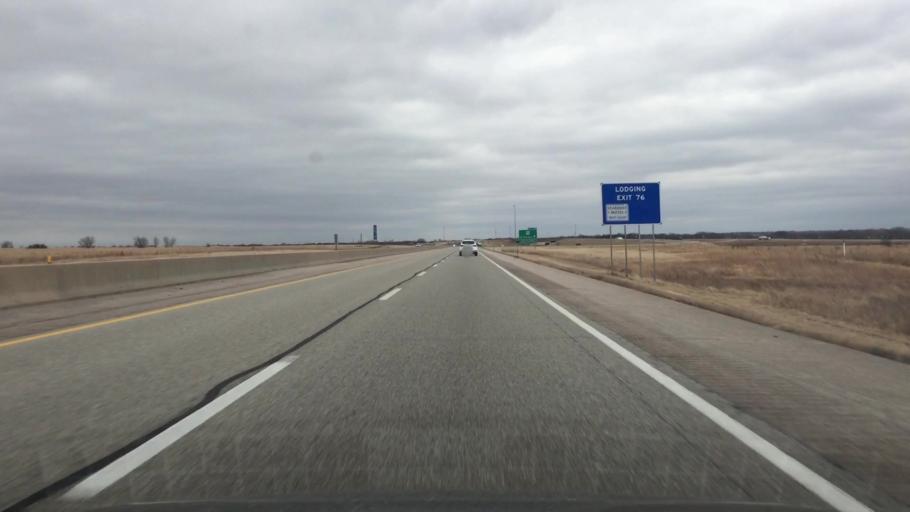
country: US
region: Kansas
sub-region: Butler County
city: El Dorado
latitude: 37.8832
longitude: -96.8416
